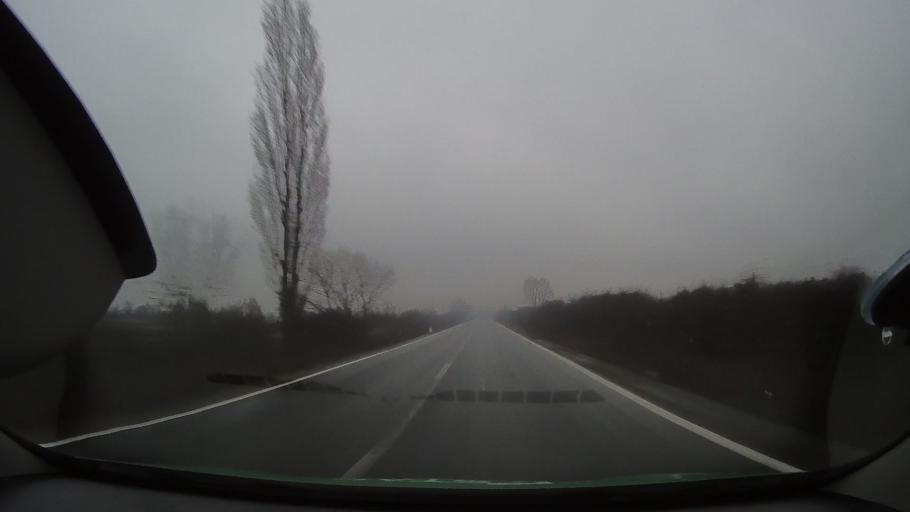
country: RO
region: Bihor
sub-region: Comuna Tinca
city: Tinca
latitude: 46.7473
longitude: 21.9384
